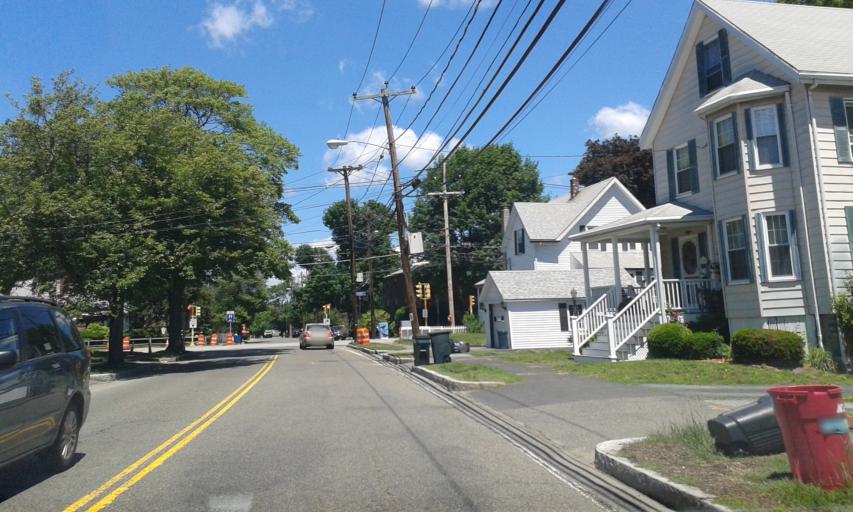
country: US
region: Massachusetts
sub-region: Middlesex County
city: Stoneham
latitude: 42.4724
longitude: -71.1066
